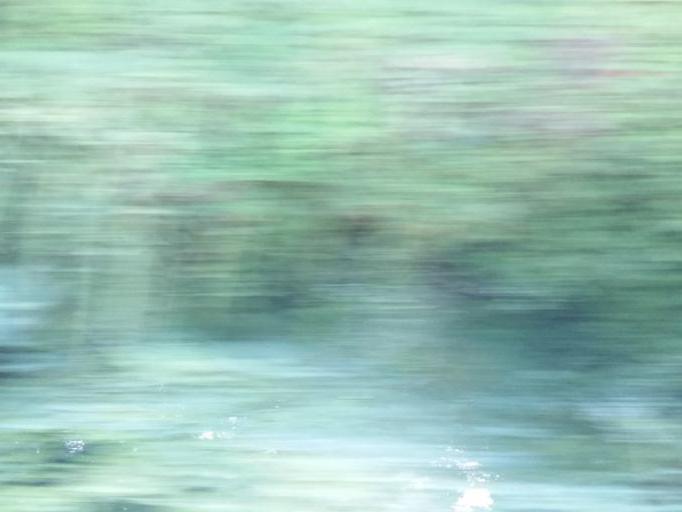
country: US
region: Tennessee
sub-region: Knox County
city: Knoxville
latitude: 35.9053
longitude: -83.9130
